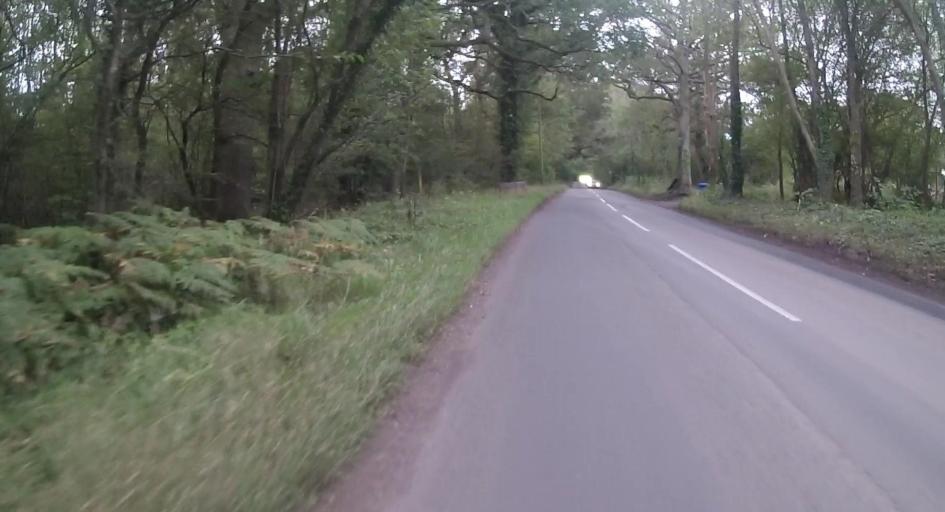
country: GB
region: England
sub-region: Hampshire
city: Fleet
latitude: 51.2516
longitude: -0.8633
